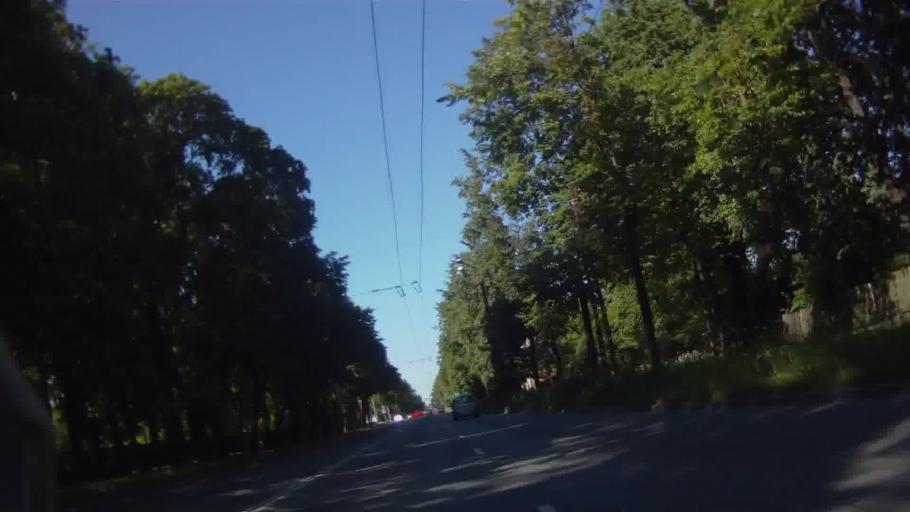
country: LV
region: Riga
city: Riga
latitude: 56.9145
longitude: 24.0873
